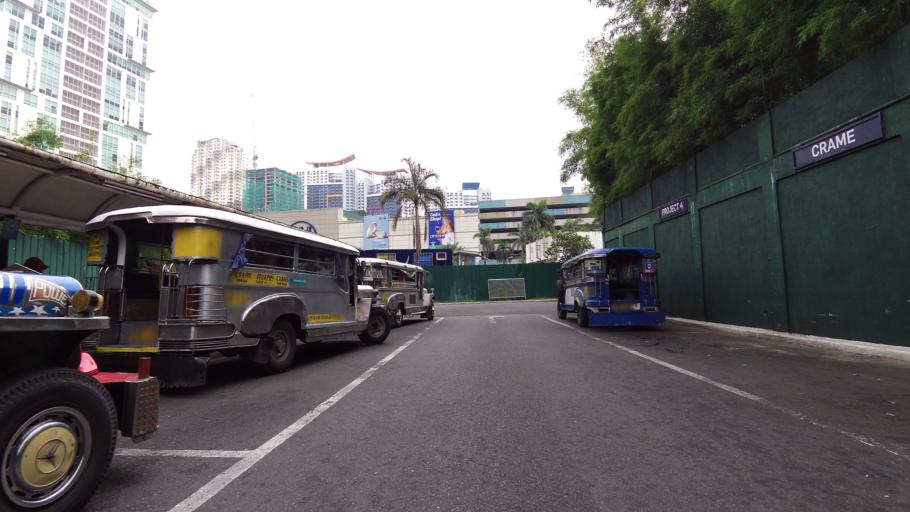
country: PH
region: Metro Manila
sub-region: San Juan
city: San Juan
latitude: 14.6178
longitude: 121.0545
